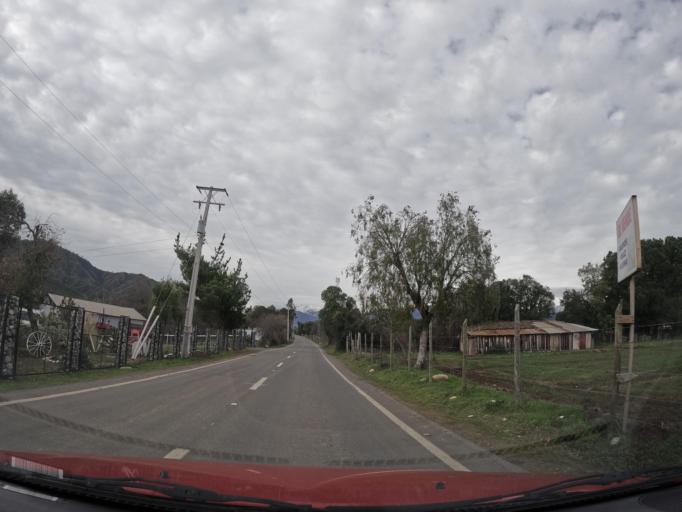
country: CL
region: Maule
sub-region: Provincia de Linares
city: Linares
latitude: -35.9237
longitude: -71.4108
